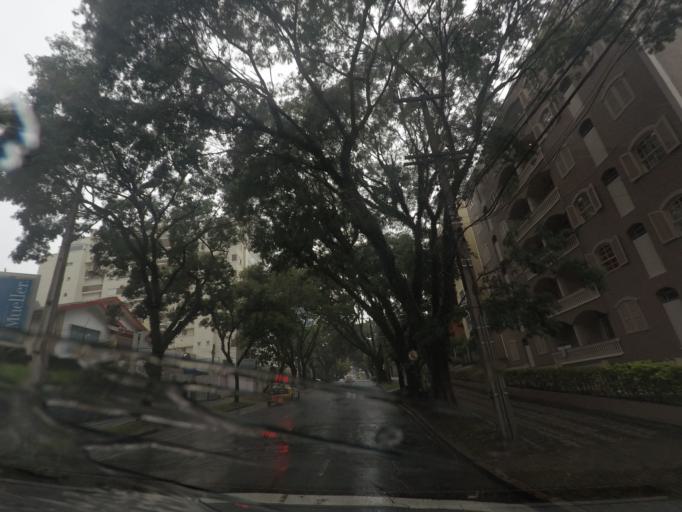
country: BR
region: Parana
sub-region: Curitiba
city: Curitiba
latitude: -25.4233
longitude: -49.2870
